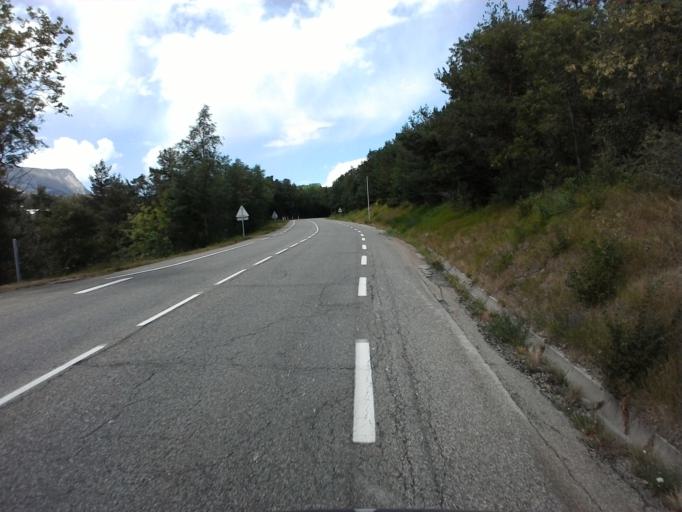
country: FR
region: Provence-Alpes-Cote d'Azur
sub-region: Departement des Hautes-Alpes
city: Gap
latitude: 44.5933
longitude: 6.0808
